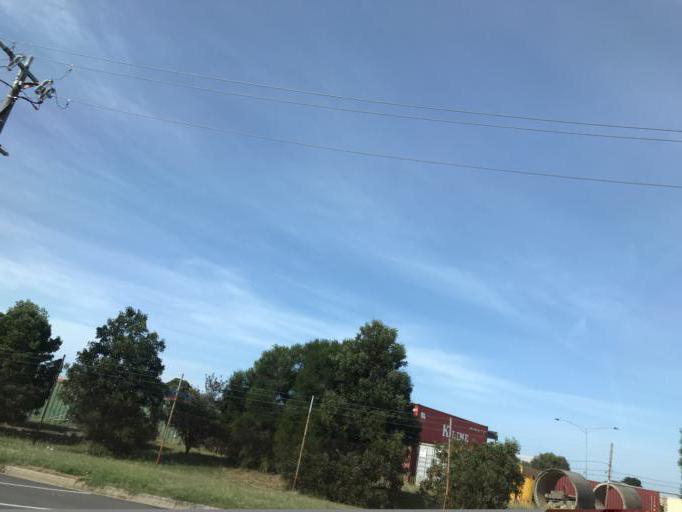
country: AU
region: Victoria
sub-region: Ballarat North
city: Newington
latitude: -37.5333
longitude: 143.8100
